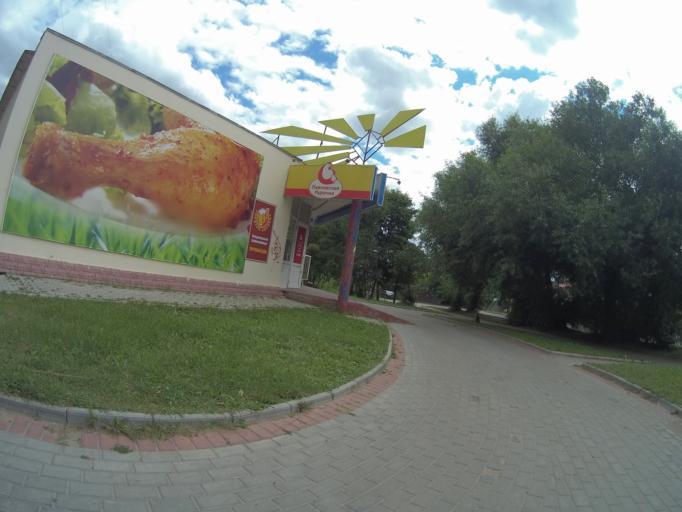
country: RU
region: Vladimir
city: Vladimir
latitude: 56.1169
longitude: 40.3732
